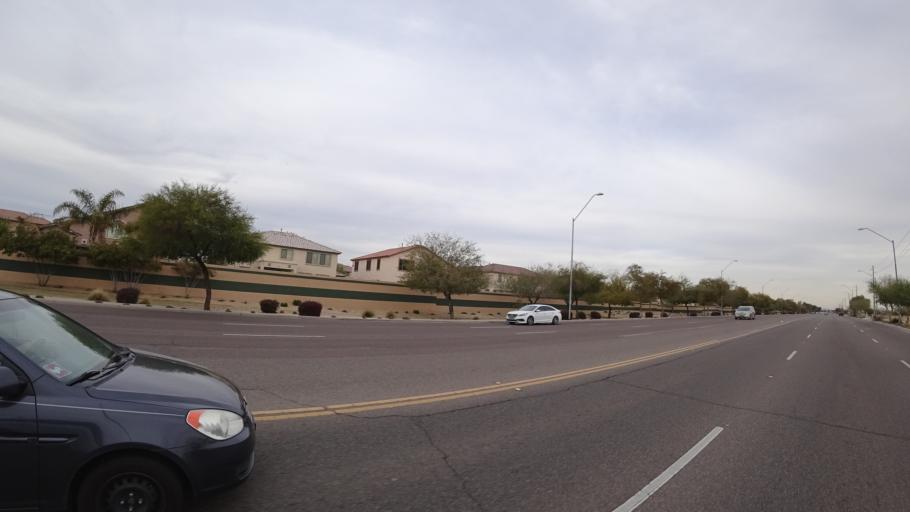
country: US
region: Arizona
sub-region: Maricopa County
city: El Mirage
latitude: 33.6091
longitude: -112.3543
